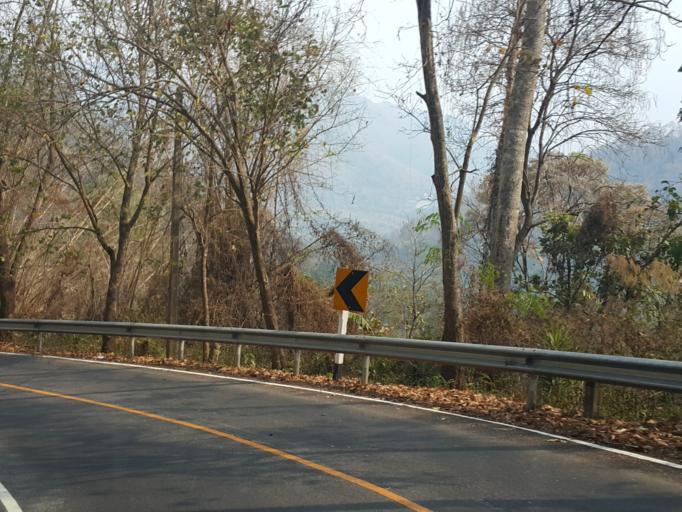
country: TH
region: Chiang Mai
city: Samoeng
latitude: 18.9089
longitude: 98.8275
